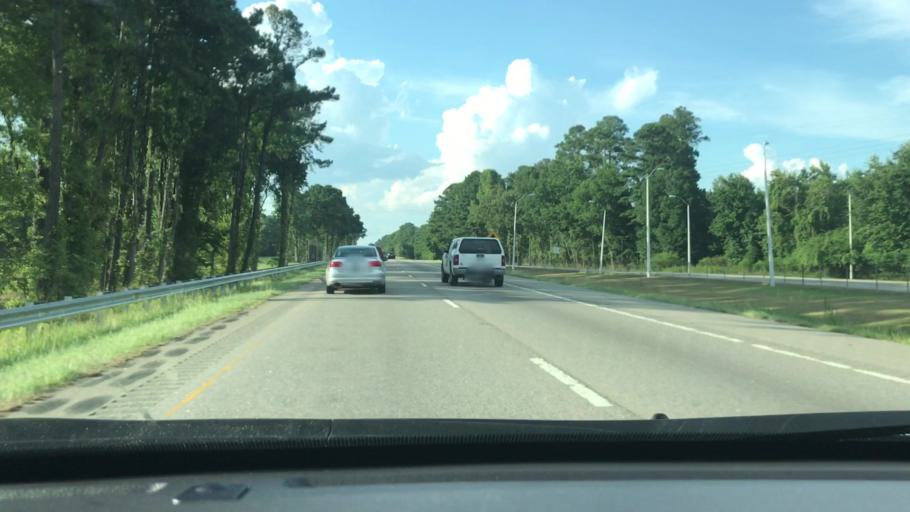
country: US
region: North Carolina
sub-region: Robeson County
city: Lumberton
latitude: 34.7065
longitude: -78.9977
